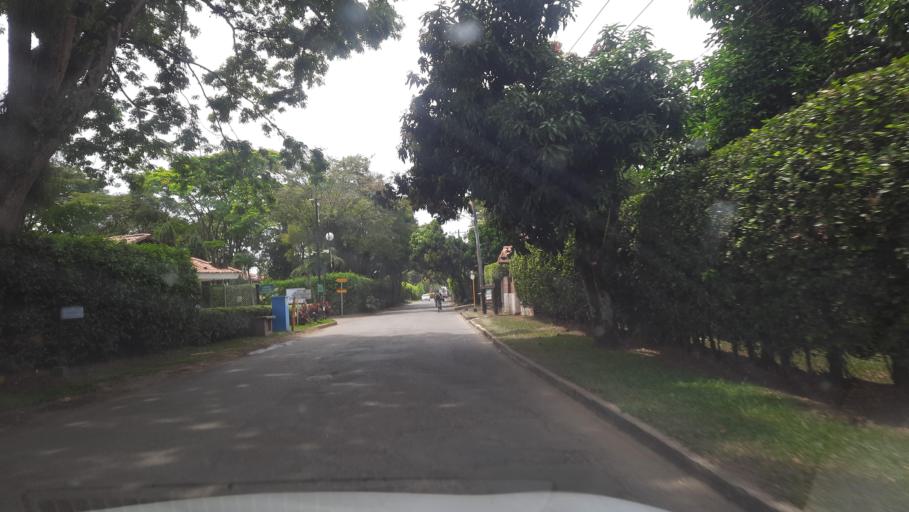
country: CO
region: Valle del Cauca
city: Jamundi
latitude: 3.2701
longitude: -76.5271
